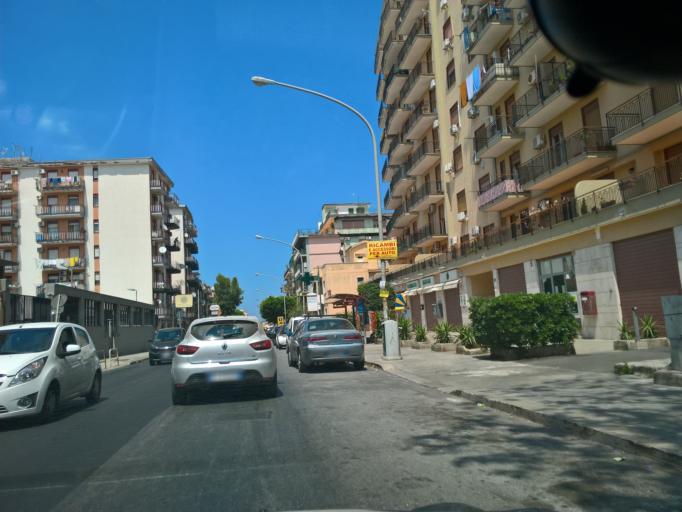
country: IT
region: Sicily
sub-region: Palermo
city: Ciaculli
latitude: 38.0913
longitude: 13.3856
